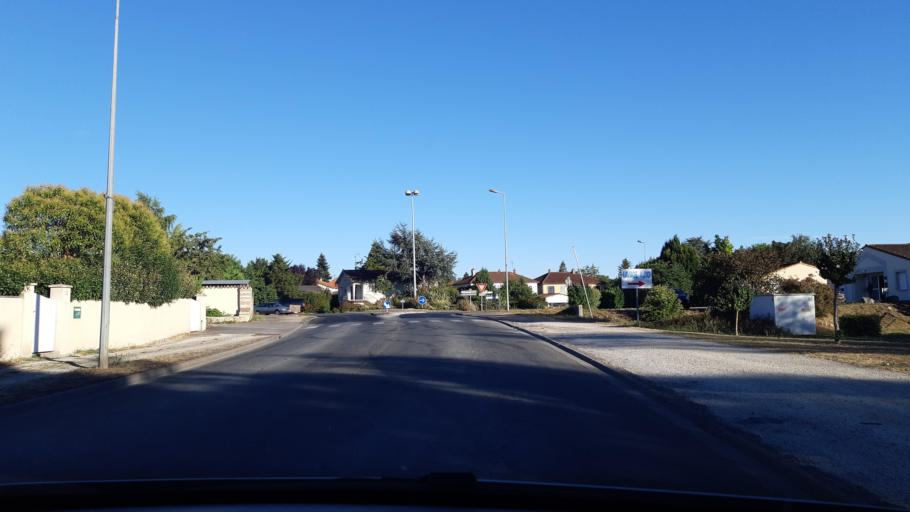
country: FR
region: Poitou-Charentes
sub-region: Departement des Deux-Sevres
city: Exireuil
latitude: 46.4198
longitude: -0.2061
